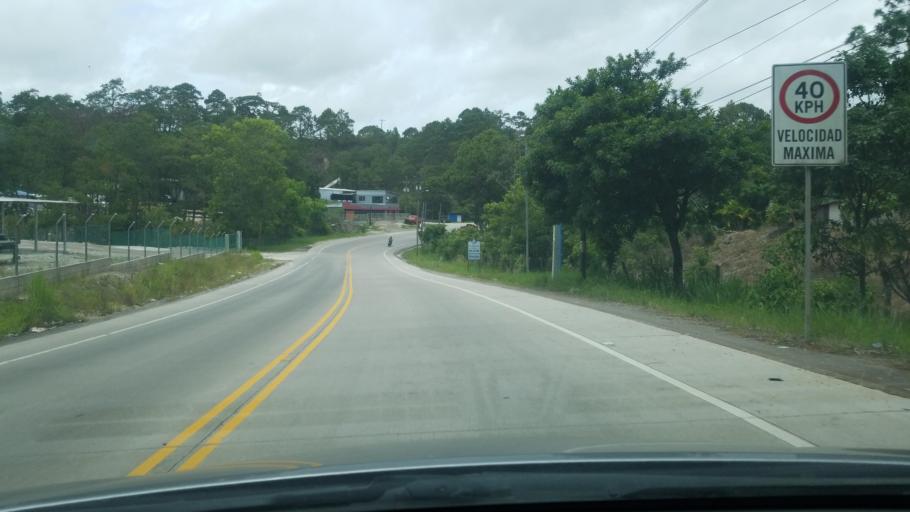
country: HN
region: Copan
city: Santa Rosa de Copan
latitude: 14.8008
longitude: -88.7762
